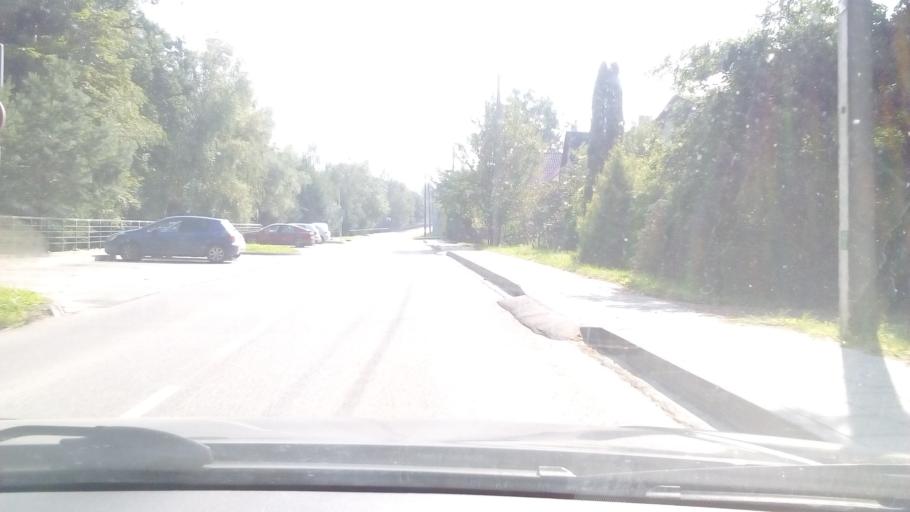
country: LT
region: Alytaus apskritis
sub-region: Alytus
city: Alytus
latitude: 54.3908
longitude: 24.0604
